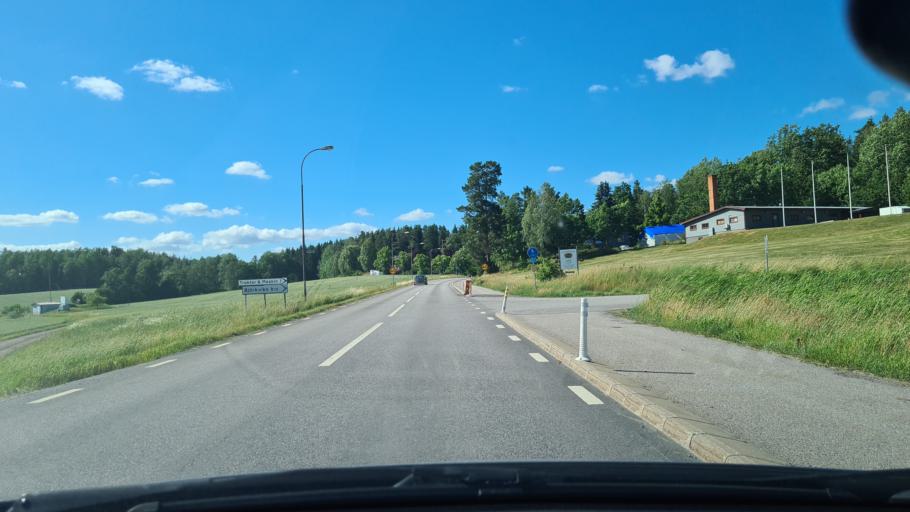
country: SE
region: Soedermanland
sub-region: Nykopings Kommun
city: Olstorp
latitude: 58.8322
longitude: 16.5166
